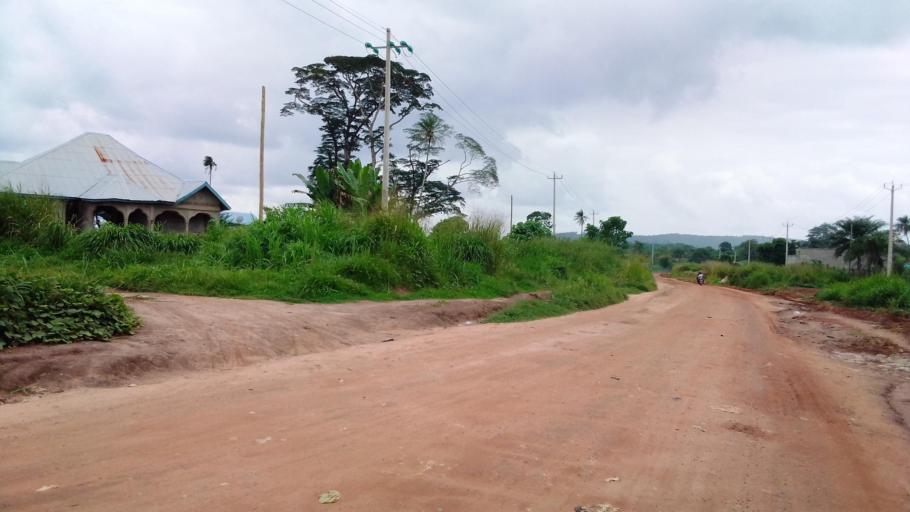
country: SL
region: Eastern Province
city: Kenema
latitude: 7.8319
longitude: -11.1819
